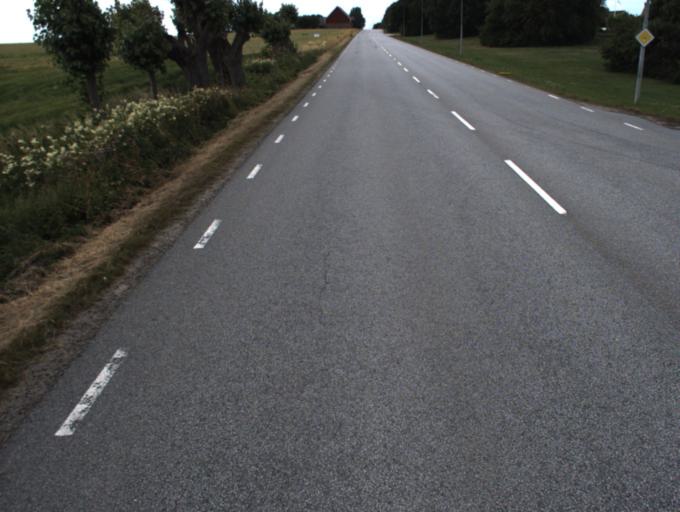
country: SE
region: Skane
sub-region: Helsingborg
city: Rydeback
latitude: 55.9581
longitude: 12.7751
